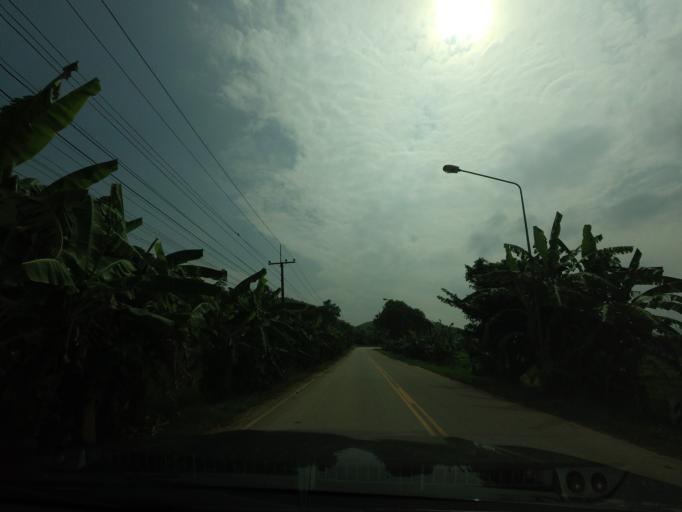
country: TH
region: Loei
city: Tha Li
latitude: 17.6617
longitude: 101.3565
